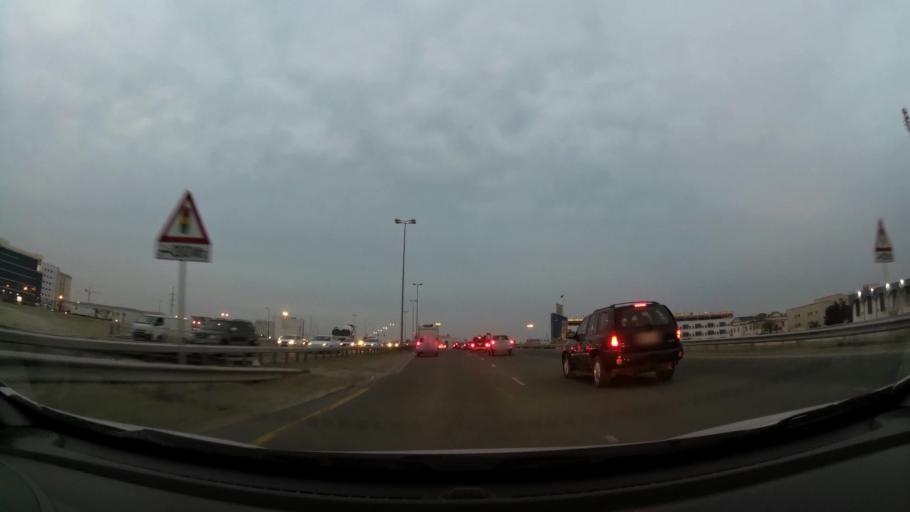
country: BH
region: Northern
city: Ar Rifa'
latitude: 26.1496
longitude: 50.5755
